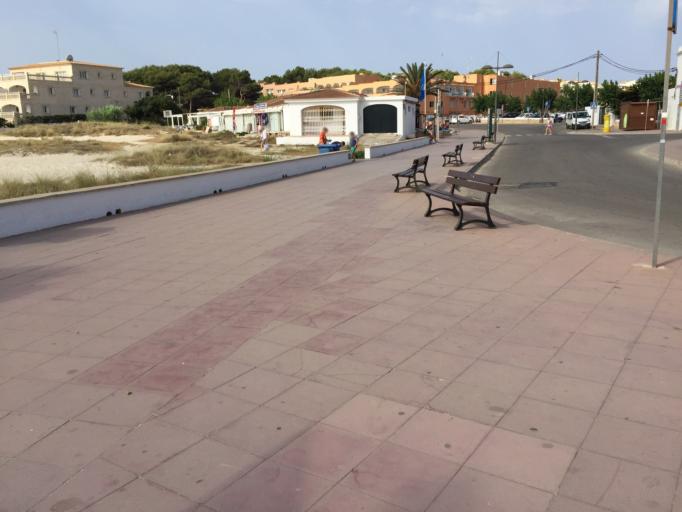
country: ES
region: Balearic Islands
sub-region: Illes Balears
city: Sant Lluis
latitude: 39.8141
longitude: 4.2799
